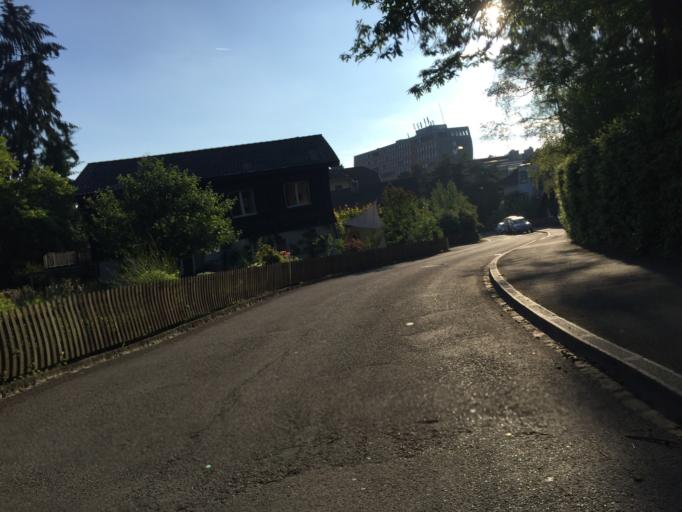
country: CH
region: Bern
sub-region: Bern-Mittelland District
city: Koniz
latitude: 46.9395
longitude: 7.4153
